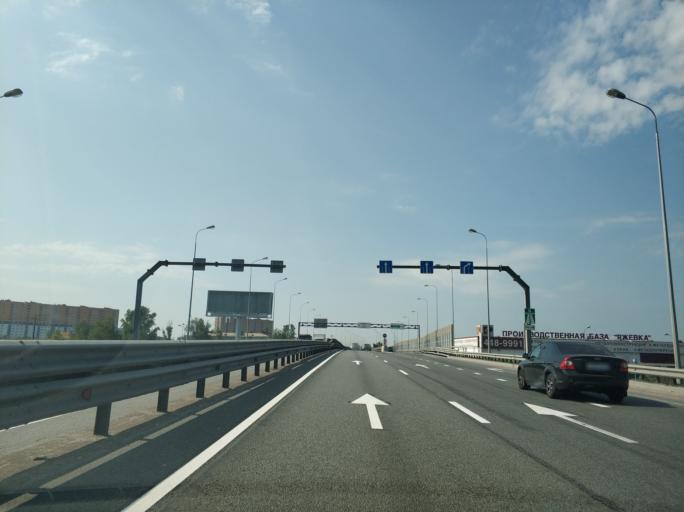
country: RU
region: St.-Petersburg
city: Krasnogvargeisky
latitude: 59.9849
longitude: 30.5169
